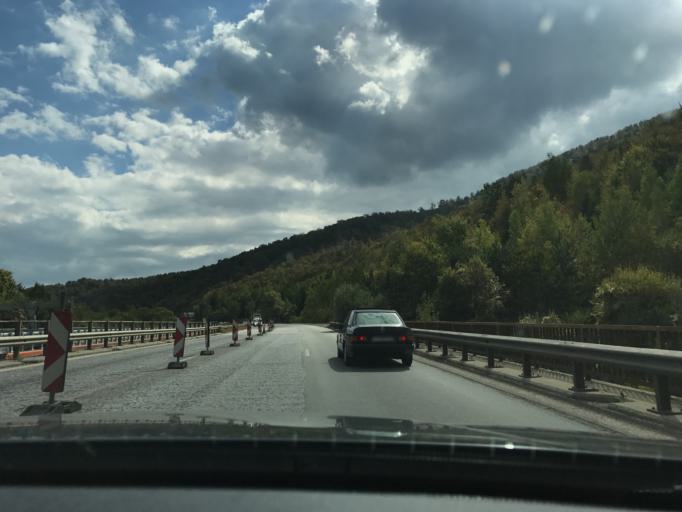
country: BG
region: Sofiya
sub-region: Obshtina Botevgrad
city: Botevgrad
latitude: 42.8155
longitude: 23.7984
